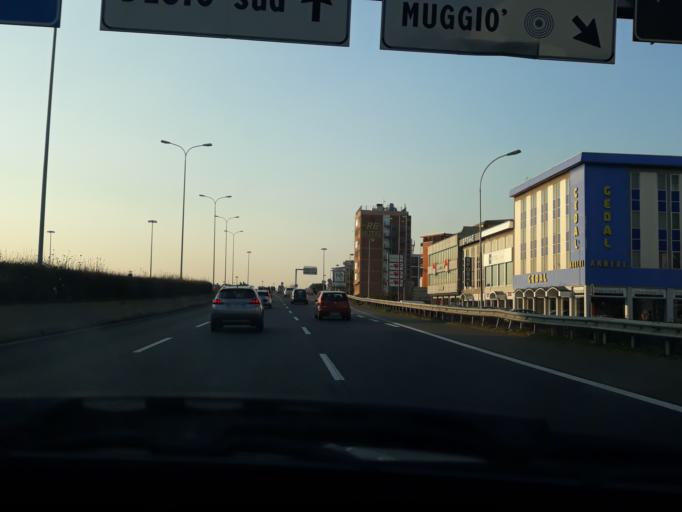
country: IT
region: Lombardy
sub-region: Provincia di Monza e Brianza
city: Lissone
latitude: 45.5989
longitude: 9.2389
